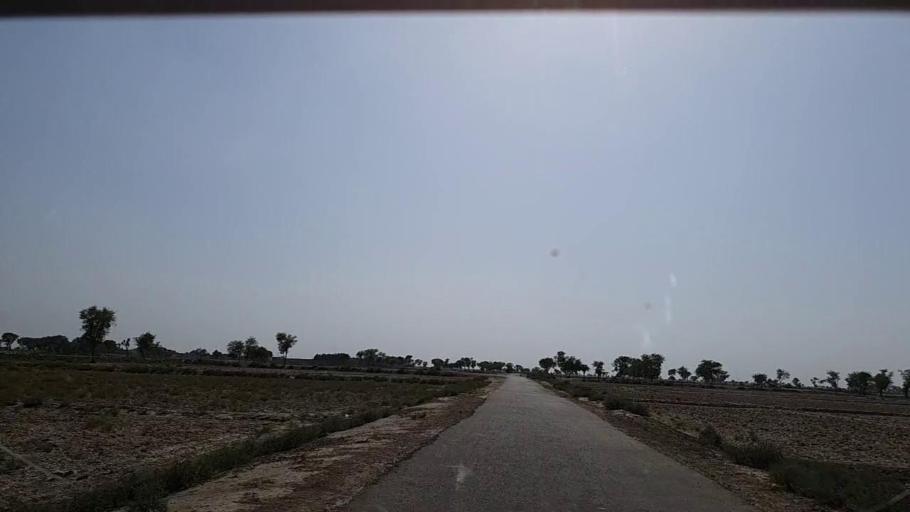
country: PK
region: Sindh
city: Phulji
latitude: 26.9243
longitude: 67.6800
